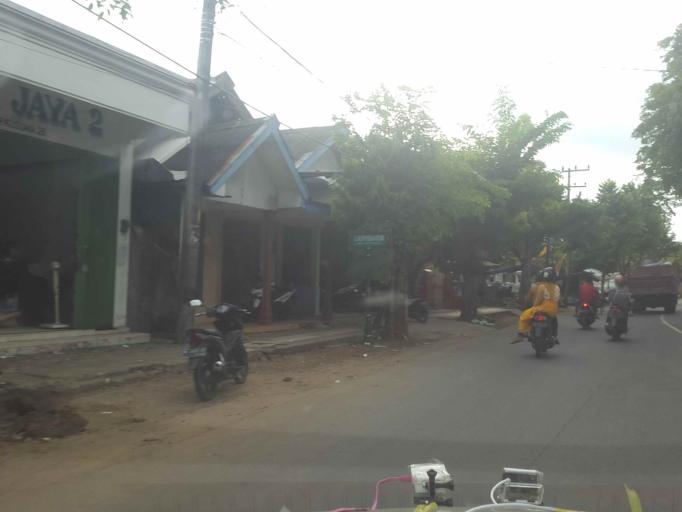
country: ID
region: East Java
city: Padusan
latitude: -7.0002
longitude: 113.8651
